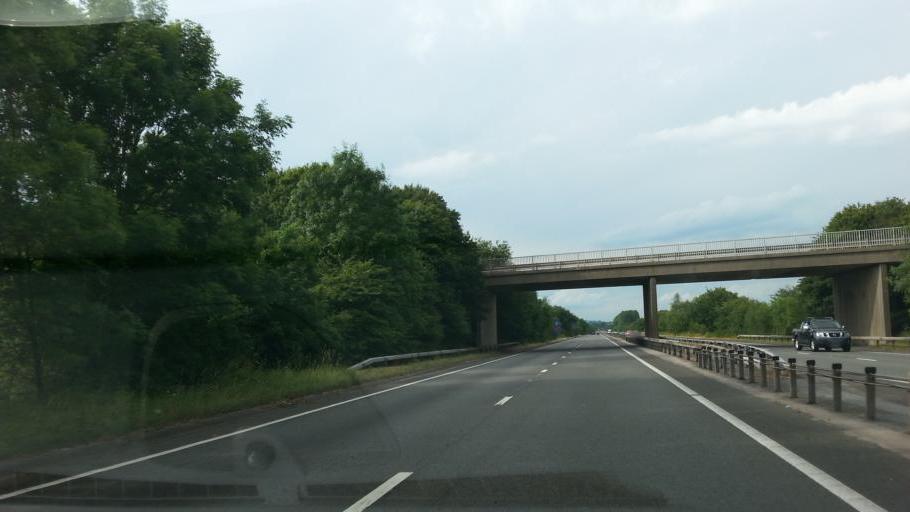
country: GB
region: Wales
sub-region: Monmouthshire
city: Llangwm
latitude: 51.7436
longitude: -2.8417
